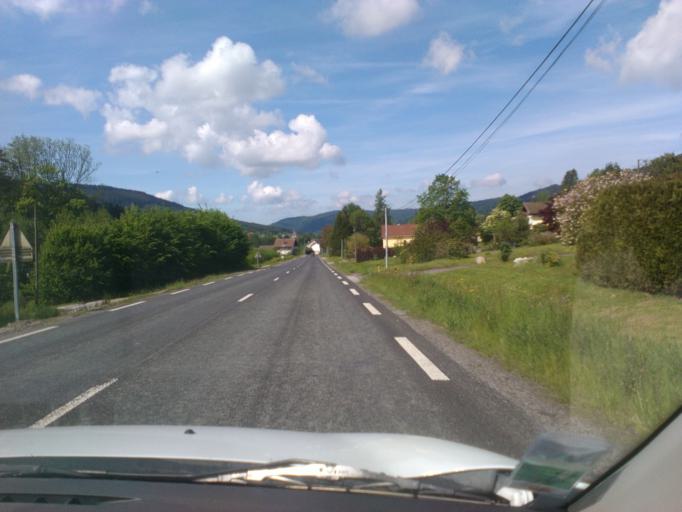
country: FR
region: Lorraine
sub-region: Departement des Vosges
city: Le Tholy
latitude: 48.0670
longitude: 6.7295
